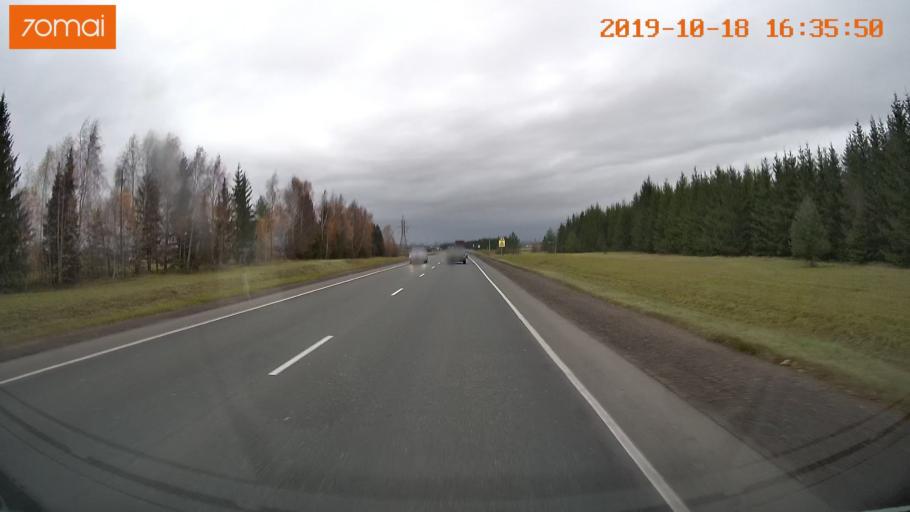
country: RU
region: Vladimir
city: Suzdal'
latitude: 56.4047
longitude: 40.4718
